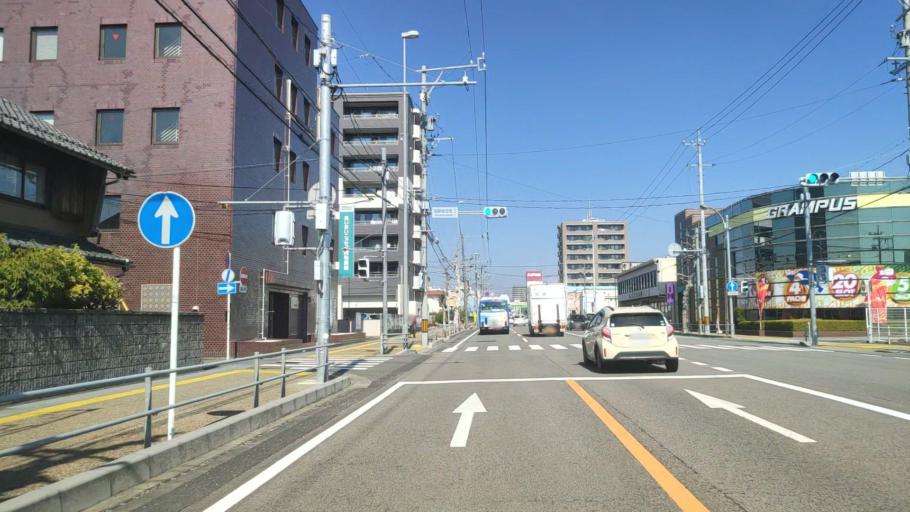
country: JP
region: Gifu
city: Gifu-shi
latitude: 35.4028
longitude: 136.7474
